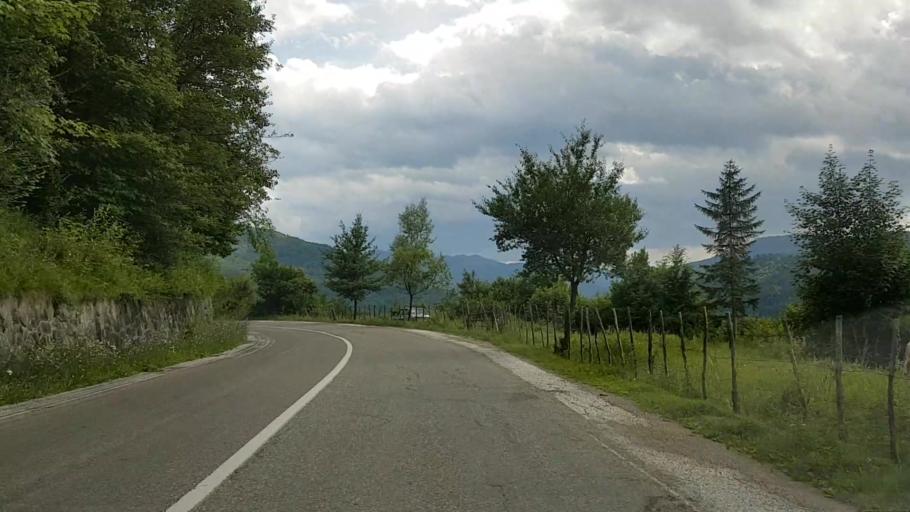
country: RO
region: Neamt
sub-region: Comuna Pangarati
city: Pangarati
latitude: 46.9614
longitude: 26.1224
